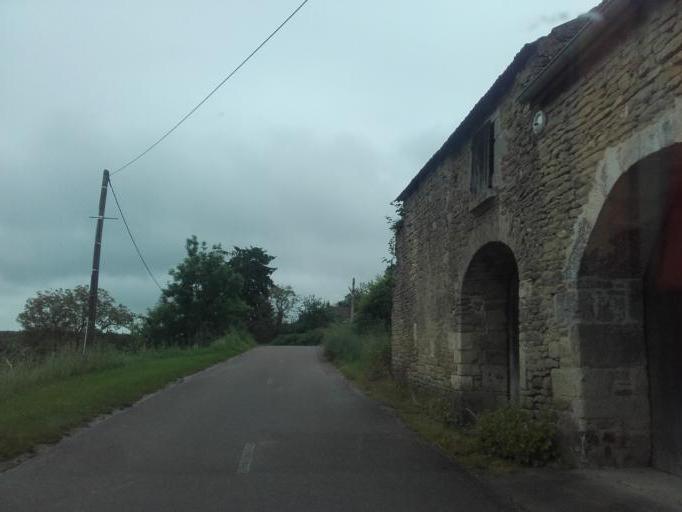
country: FR
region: Bourgogne
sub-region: Departement de la Cote-d'Or
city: Nolay
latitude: 46.9717
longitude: 4.6821
